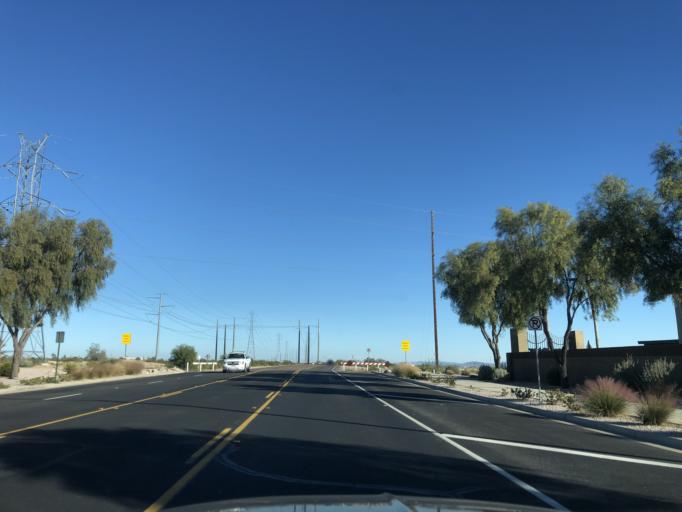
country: US
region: Arizona
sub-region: Maricopa County
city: Buckeye
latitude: 33.4204
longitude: -112.6003
